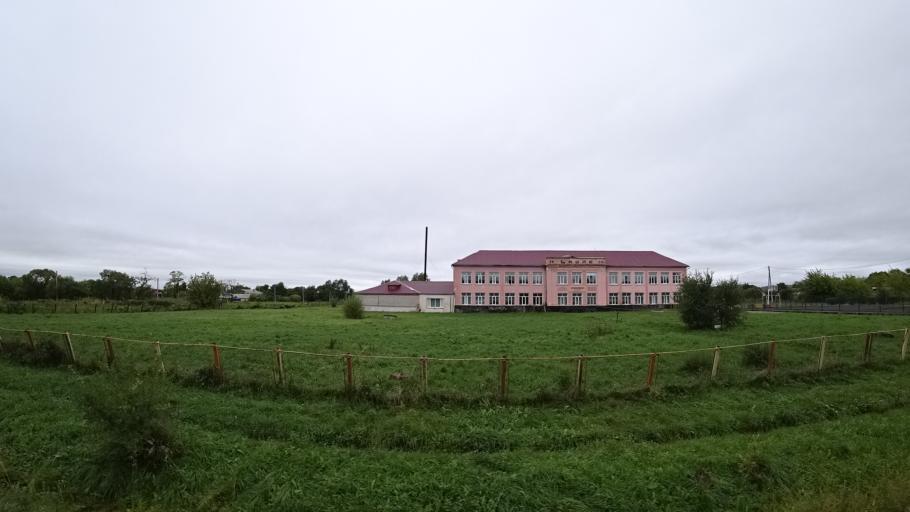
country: RU
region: Primorskiy
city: Monastyrishche
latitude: 44.1940
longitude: 132.4951
